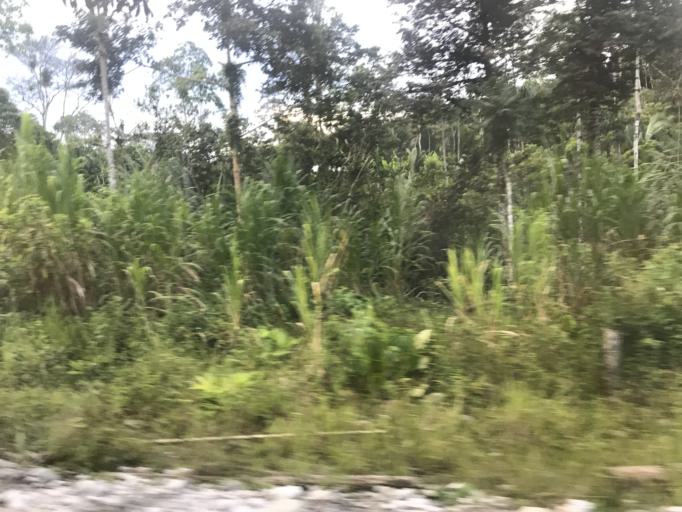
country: EC
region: Napo
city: Tena
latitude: -1.0611
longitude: -77.7008
